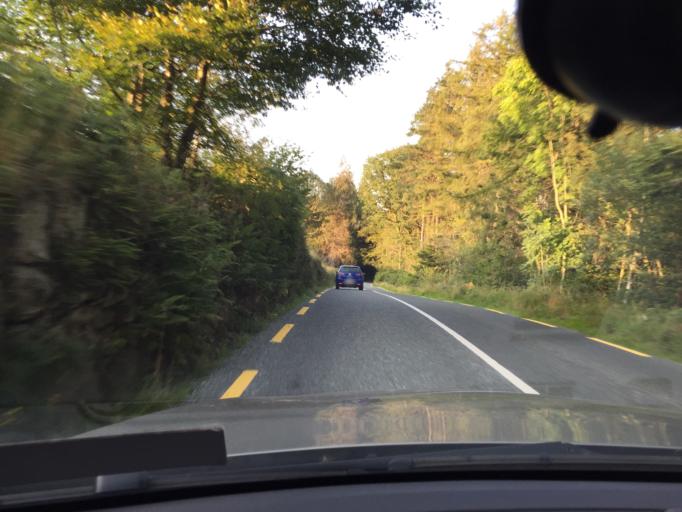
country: IE
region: Leinster
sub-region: Wicklow
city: Rathdrum
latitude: 53.0188
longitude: -6.2750
